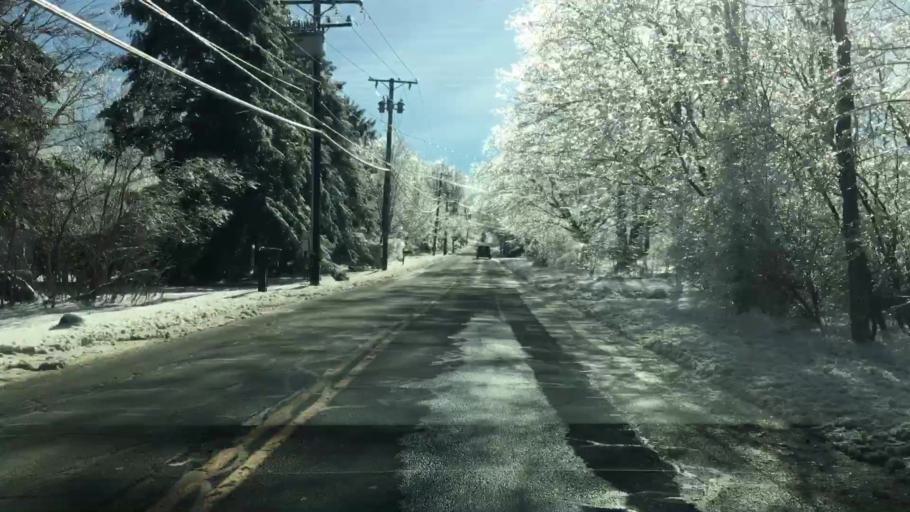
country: US
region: Connecticut
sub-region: Fairfield County
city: Newtown
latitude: 41.3925
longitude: -73.2588
